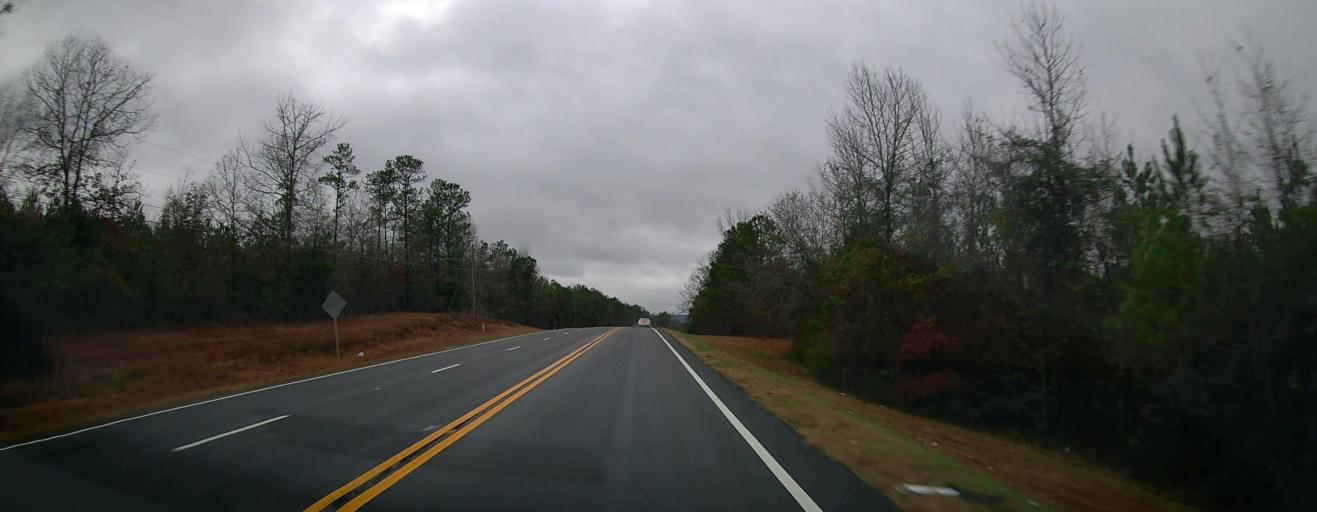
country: US
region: Alabama
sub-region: Bibb County
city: Centreville
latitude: 32.8169
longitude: -86.9368
